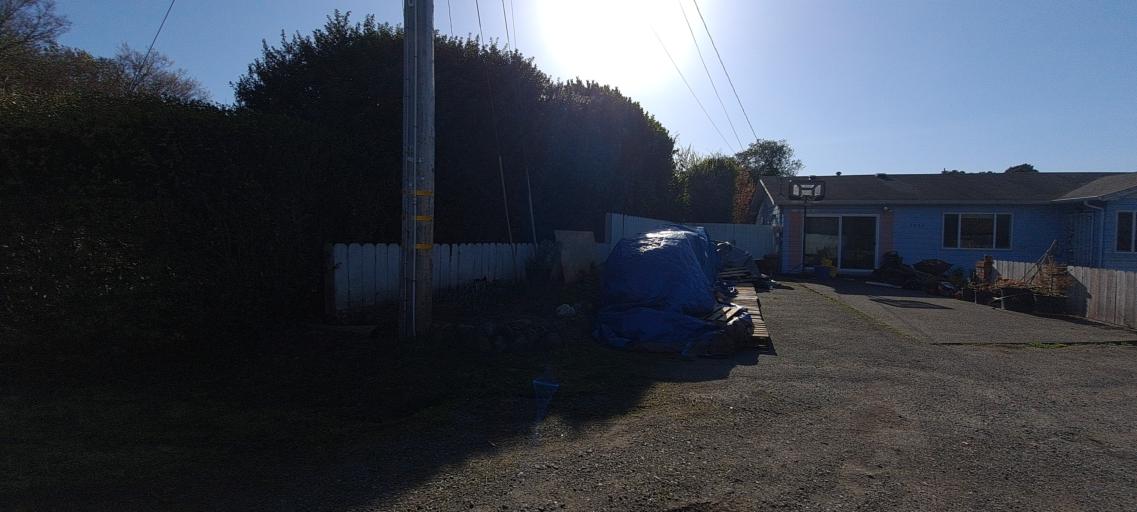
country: US
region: California
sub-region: Humboldt County
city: Fortuna
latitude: 40.5765
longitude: -124.1361
